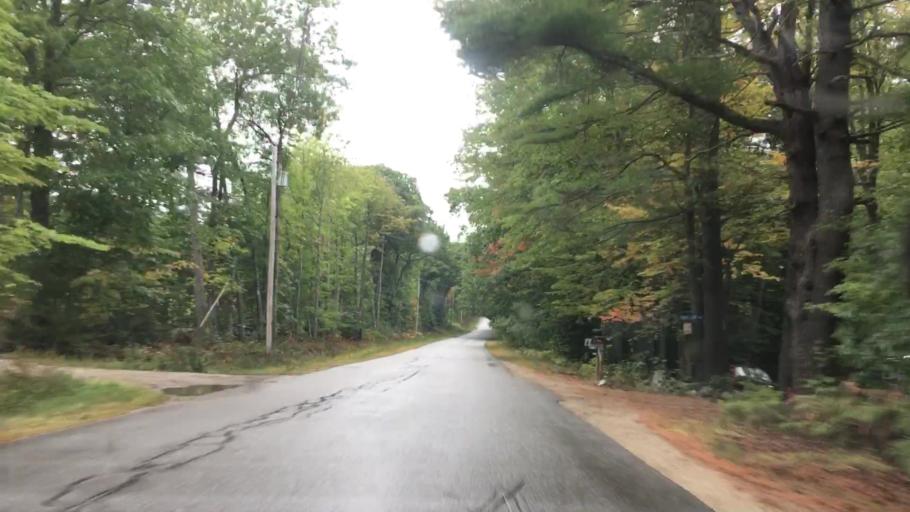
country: US
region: Maine
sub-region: Cumberland County
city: Harrison
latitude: 44.0548
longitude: -70.6187
